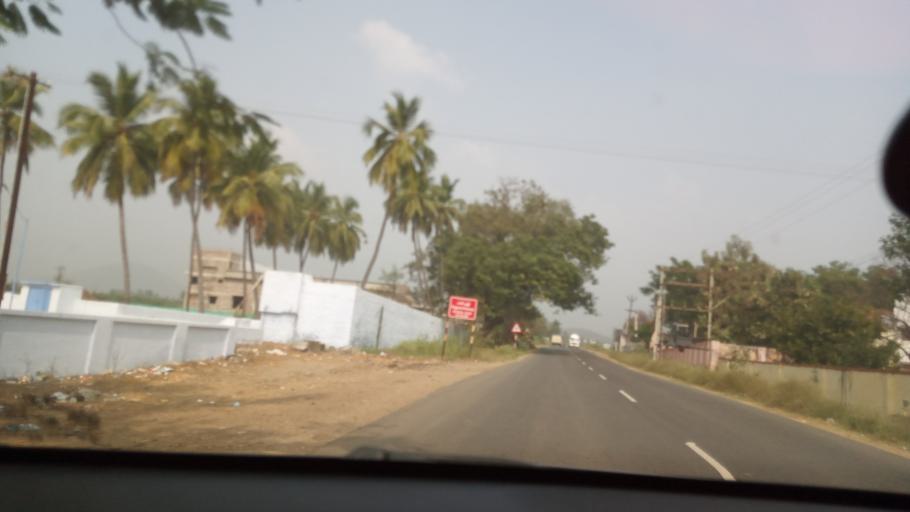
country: IN
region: Tamil Nadu
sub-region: Erode
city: Sathyamangalam
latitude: 11.5286
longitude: 77.1407
